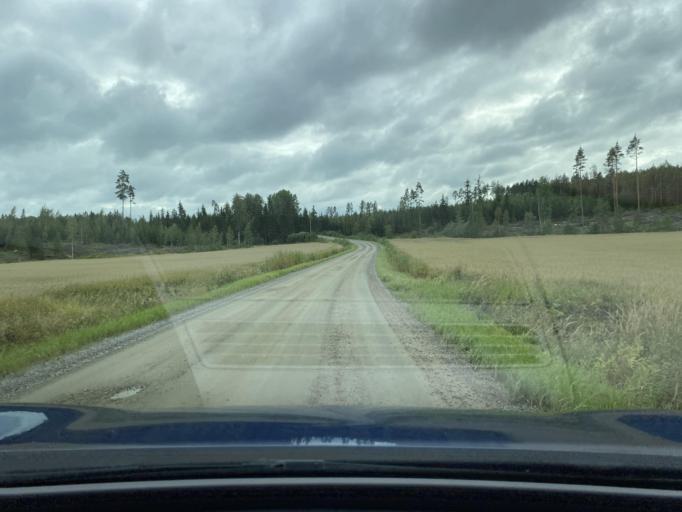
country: FI
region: Pirkanmaa
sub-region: Lounais-Pirkanmaa
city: Punkalaidun
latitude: 61.2149
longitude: 23.1691
